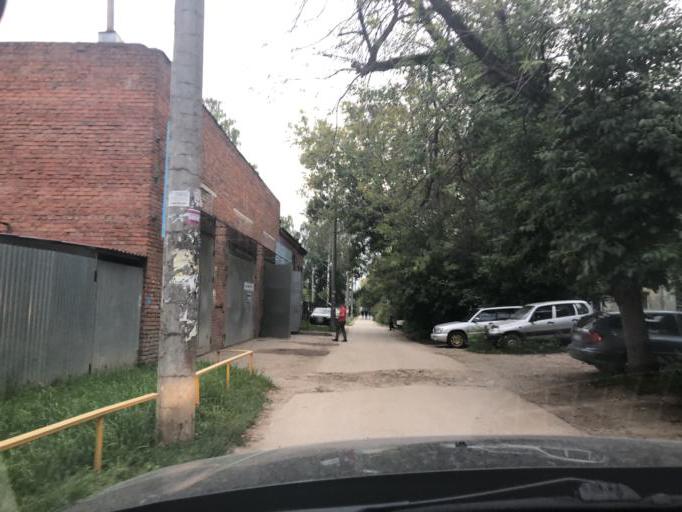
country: RU
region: Tula
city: Tula
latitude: 54.1949
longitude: 37.6732
